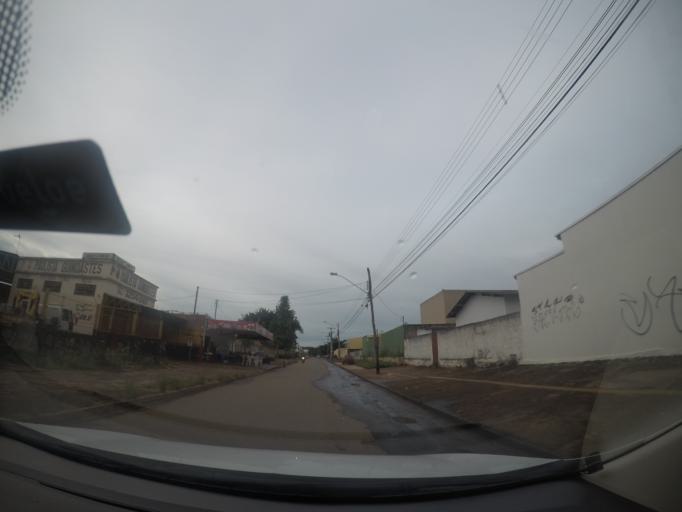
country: BR
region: Goias
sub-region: Goiania
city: Goiania
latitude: -16.6364
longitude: -49.2392
